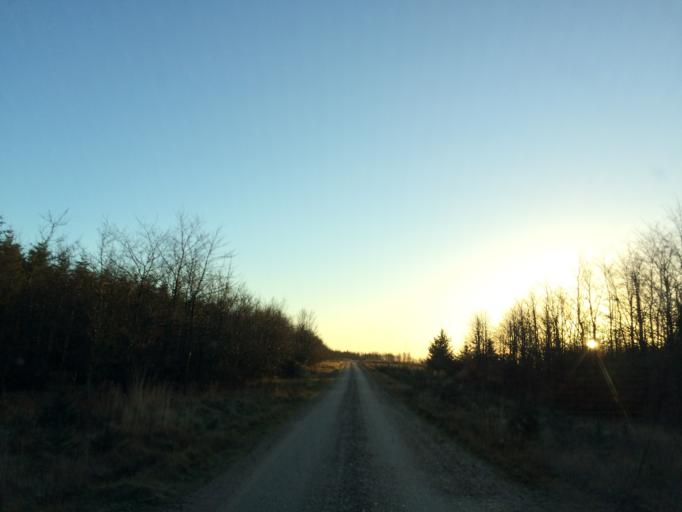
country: DK
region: Central Jutland
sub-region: Holstebro Kommune
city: Holstebro
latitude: 56.2203
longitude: 8.5125
